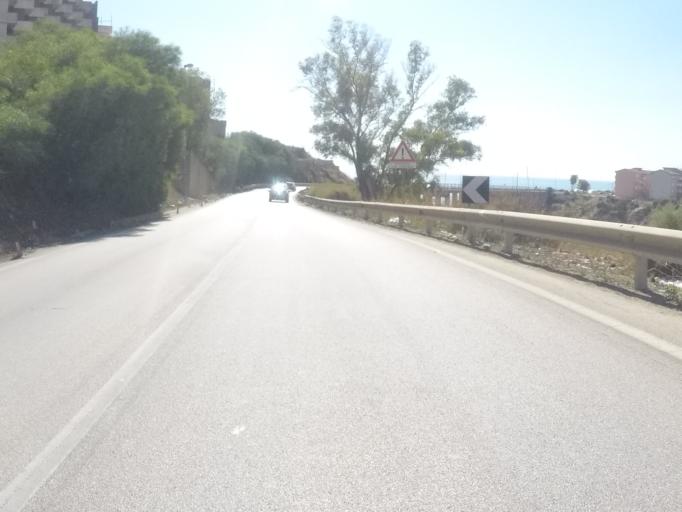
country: IT
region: Sicily
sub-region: Agrigento
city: Porto Empedocle
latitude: 37.2932
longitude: 13.5199
